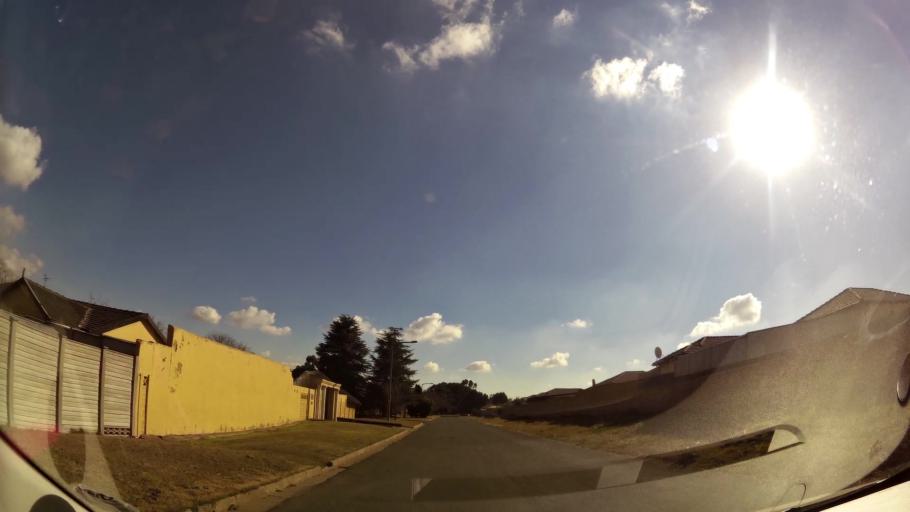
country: ZA
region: Gauteng
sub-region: City of Johannesburg Metropolitan Municipality
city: Roodepoort
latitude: -26.1413
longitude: 27.8226
